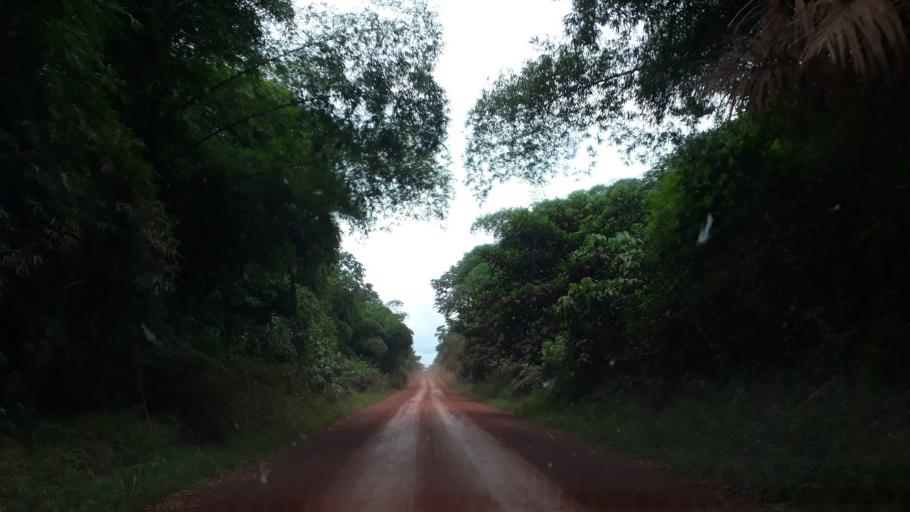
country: CD
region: Eastern Province
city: Kisangani
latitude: 0.5428
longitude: 25.8280
